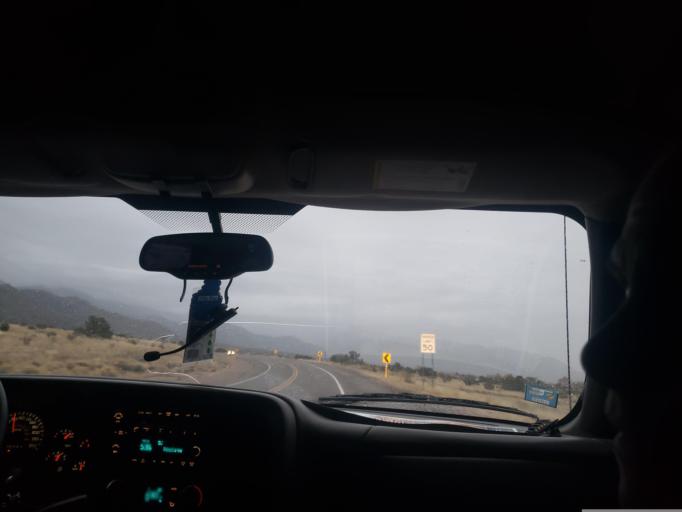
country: US
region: New Mexico
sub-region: Bernalillo County
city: Sandia Heights
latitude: 35.1973
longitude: -106.5033
